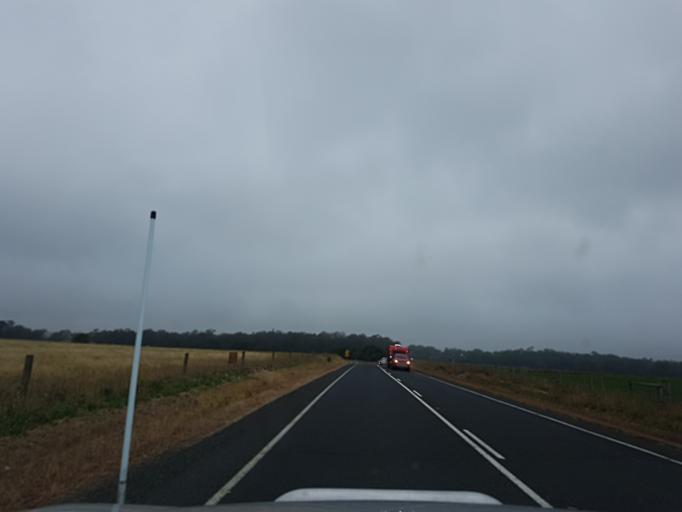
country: AU
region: Victoria
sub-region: Wellington
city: Sale
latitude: -38.0858
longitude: 147.0038
